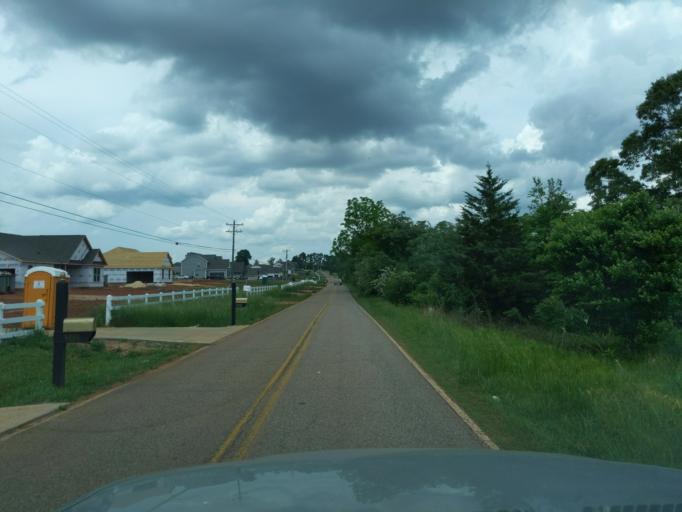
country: US
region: South Carolina
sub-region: Spartanburg County
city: Inman Mills
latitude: 35.0222
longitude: -82.1254
